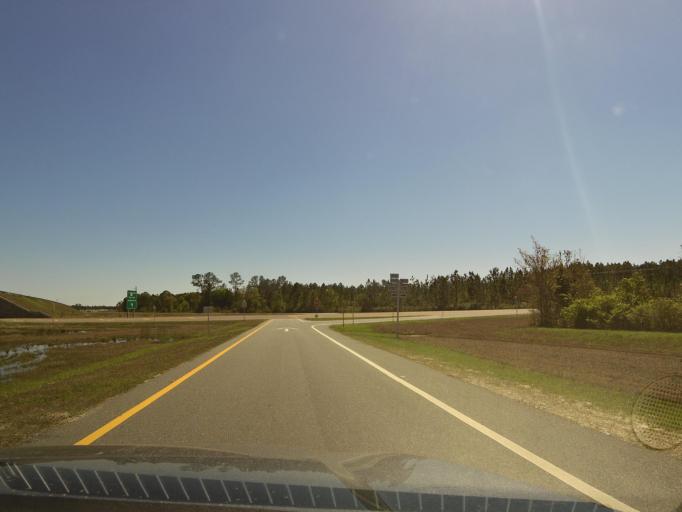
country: US
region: Florida
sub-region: Bradford County
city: Starke
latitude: 29.9469
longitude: -82.1382
